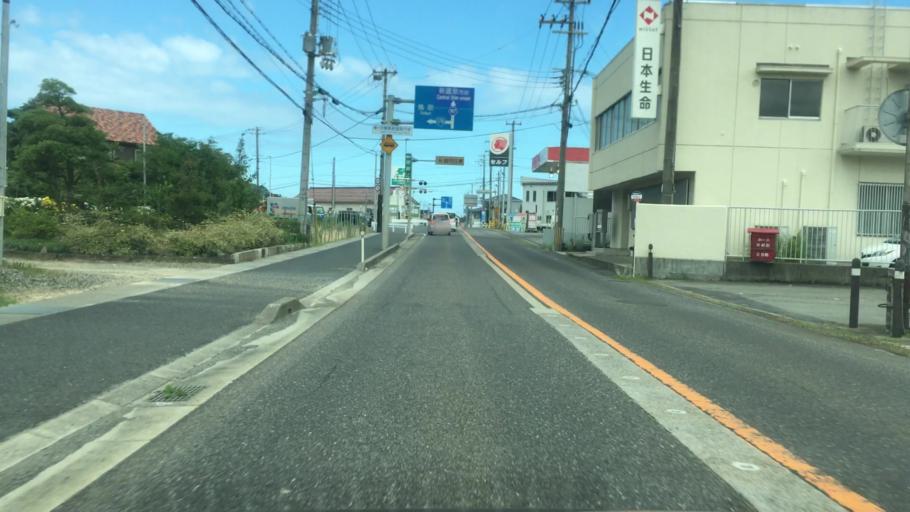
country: JP
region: Tottori
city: Tottori
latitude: 35.6184
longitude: 134.4624
